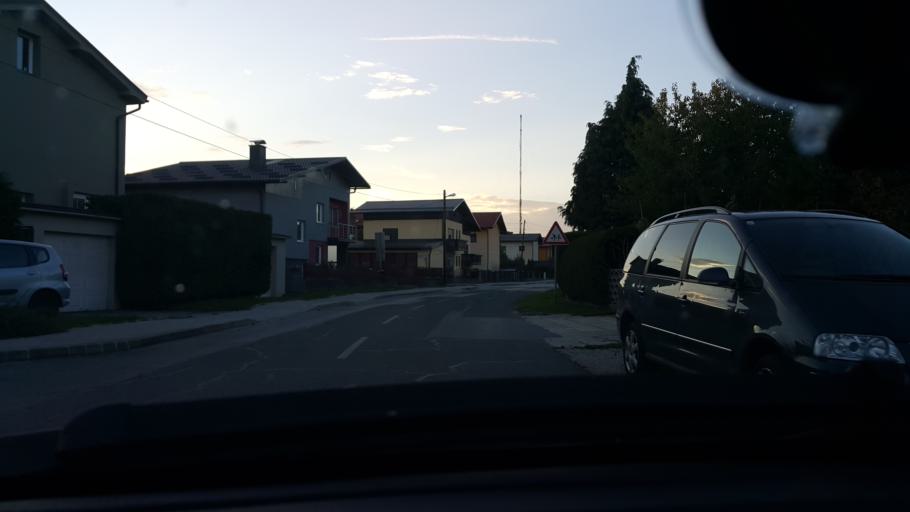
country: SI
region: Hoce-Slivnica
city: Rogoza
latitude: 46.5309
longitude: 15.6779
